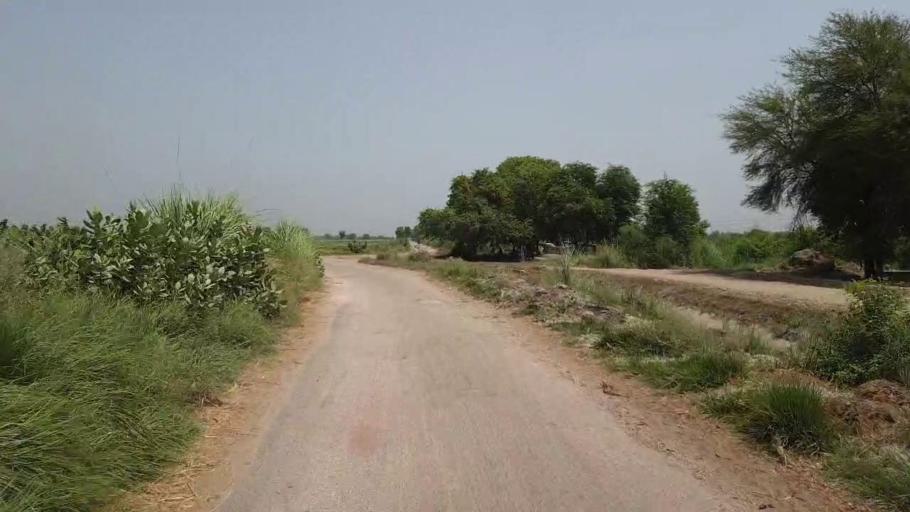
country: PK
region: Sindh
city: Nawabshah
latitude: 26.2874
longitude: 68.3096
